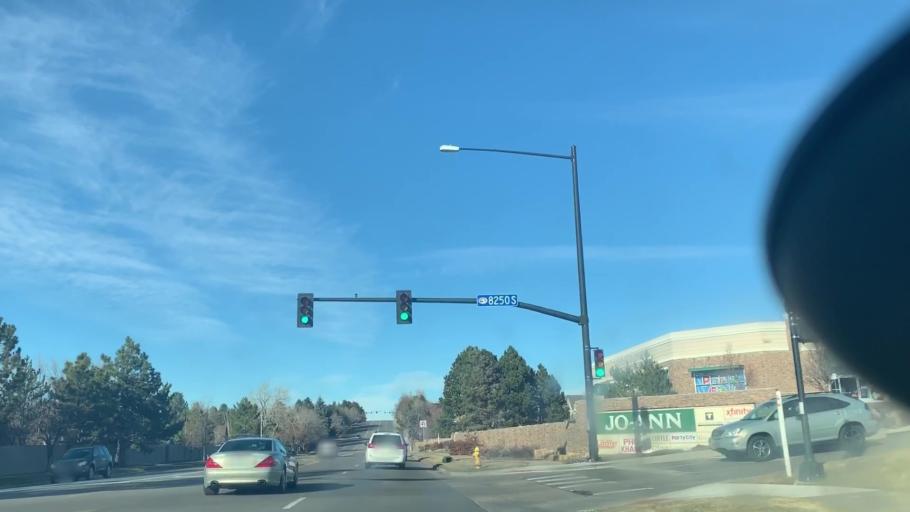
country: US
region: Colorado
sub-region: Douglas County
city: Acres Green
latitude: 39.5669
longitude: -104.8856
